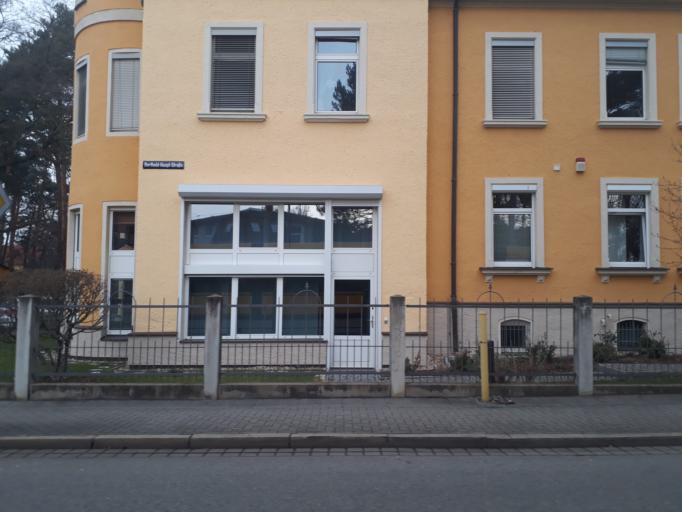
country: DE
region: Saxony
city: Heidenau
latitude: 51.0086
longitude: 13.8545
